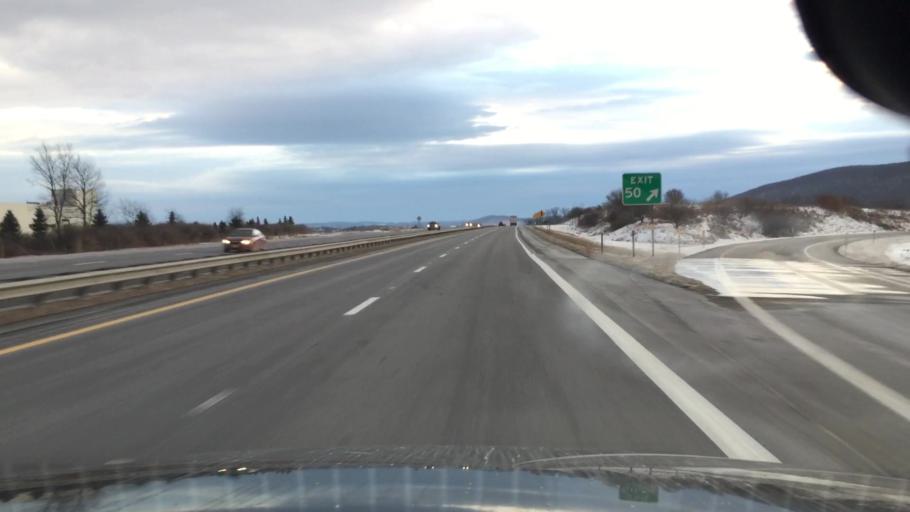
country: US
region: New York
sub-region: Chemung County
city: Big Flats
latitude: 42.1487
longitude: -76.9146
